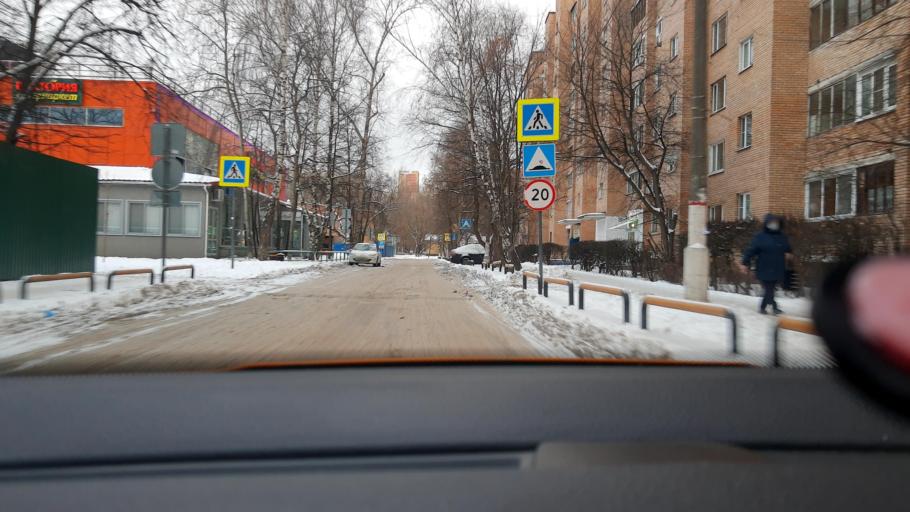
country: RU
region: Moskovskaya
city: Levoberezhnaya
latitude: 55.8910
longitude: 37.4786
